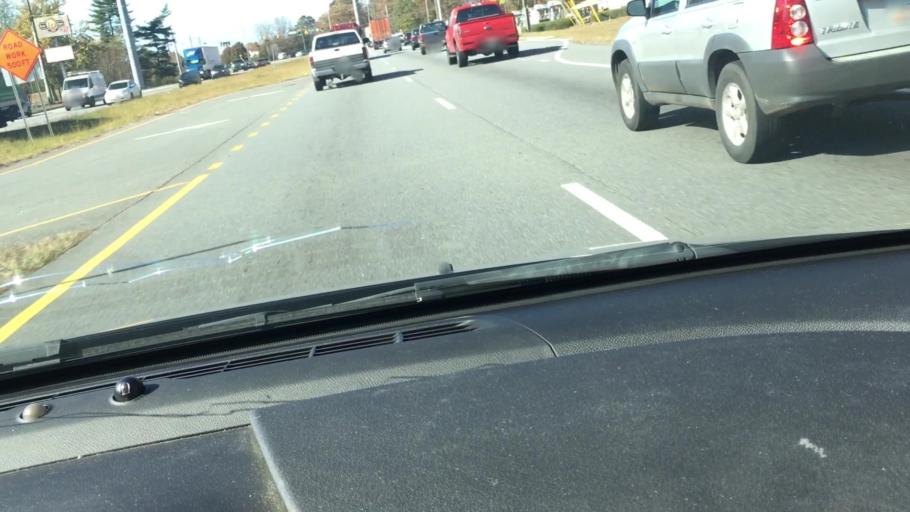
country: US
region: Georgia
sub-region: Fulton County
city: Milton
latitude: 34.1293
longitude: -84.2278
